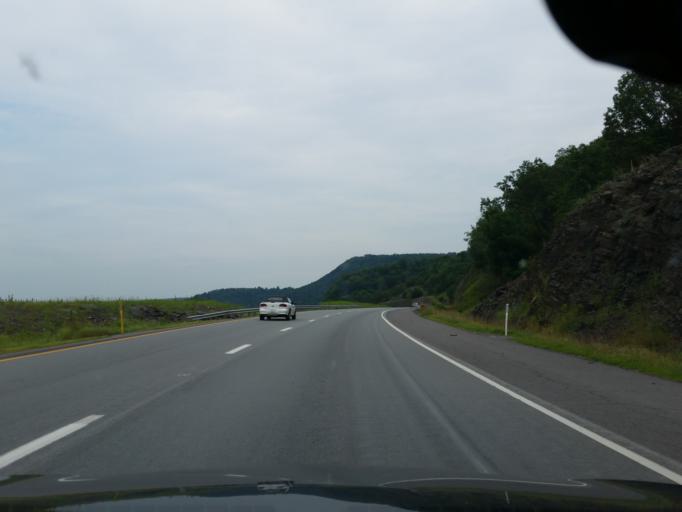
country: US
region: Pennsylvania
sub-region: Perry County
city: Duncannon
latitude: 40.4541
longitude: -77.0237
